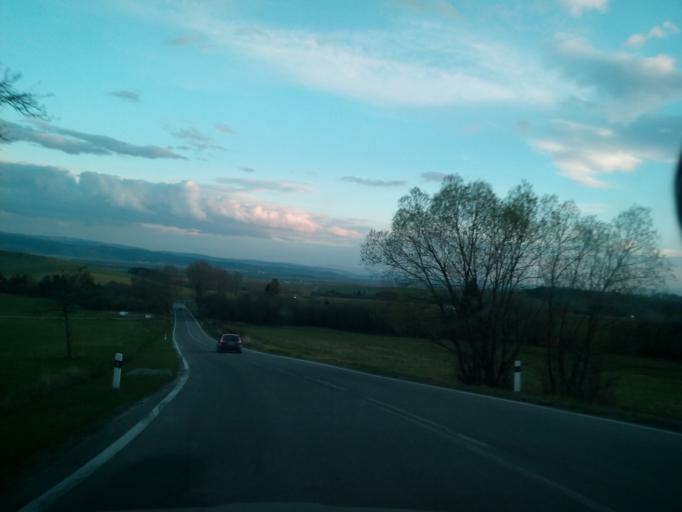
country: SK
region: Presovsky
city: Spisska Bela
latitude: 49.2653
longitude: 20.4245
